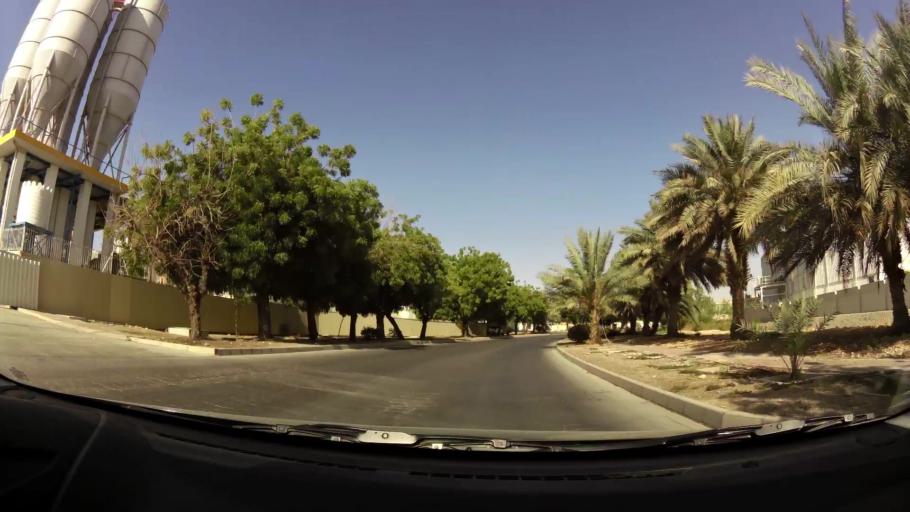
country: OM
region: Muhafazat Masqat
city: As Sib al Jadidah
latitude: 23.5562
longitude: 58.2205
